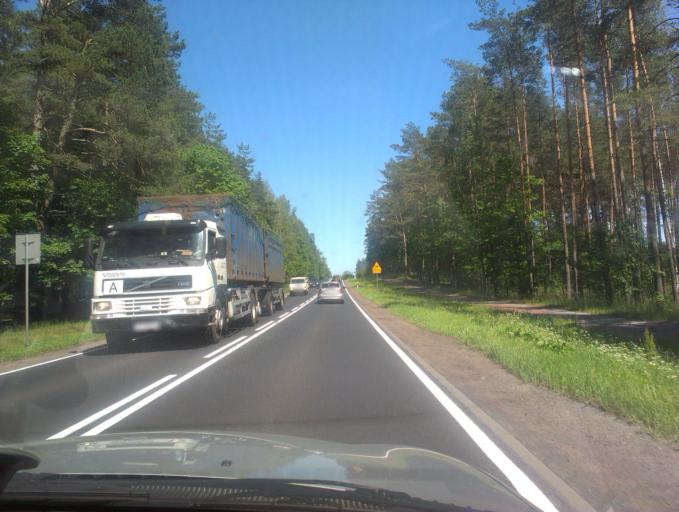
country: PL
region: Pomeranian Voivodeship
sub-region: Powiat czluchowski
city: Czluchow
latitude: 53.6820
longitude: 17.4121
